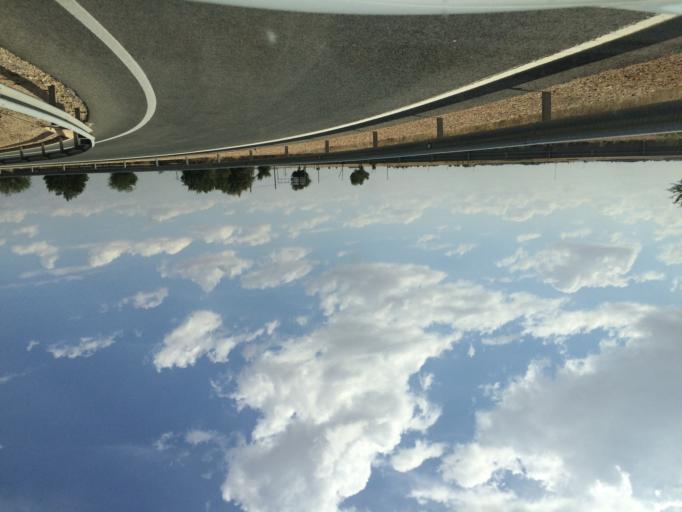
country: ES
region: Castille-La Mancha
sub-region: Provincia de Albacete
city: Albacete
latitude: 39.0017
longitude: -1.9047
